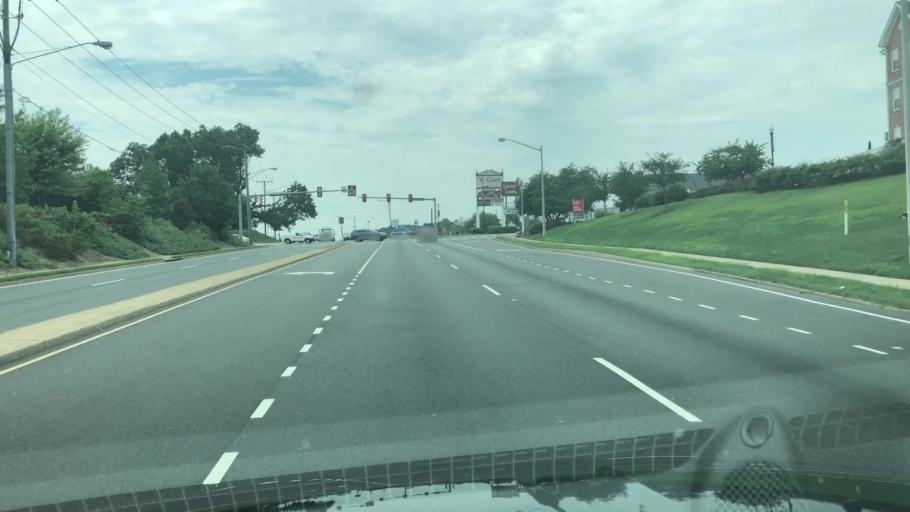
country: US
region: Virginia
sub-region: City of Fredericksburg
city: Fredericksburg
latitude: 38.3076
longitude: -77.4792
